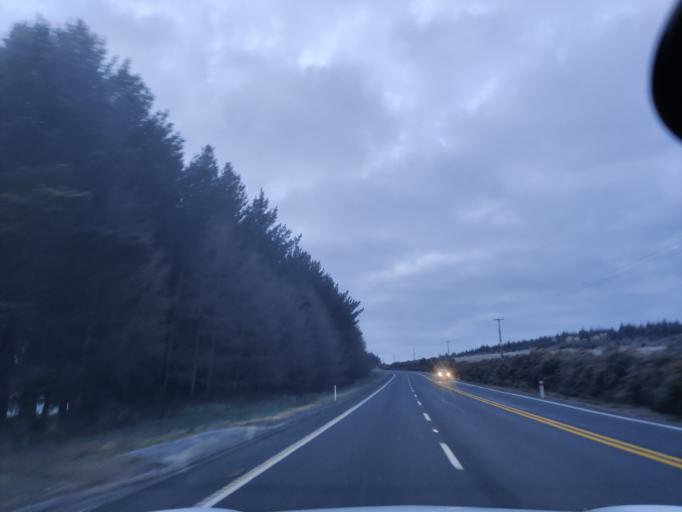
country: NZ
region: Waikato
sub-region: South Waikato District
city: Tokoroa
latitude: -38.3968
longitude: 176.0395
